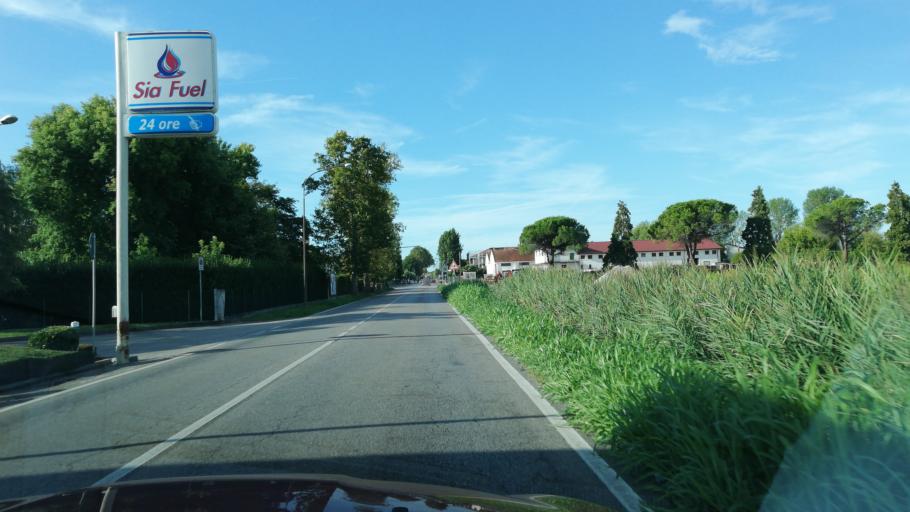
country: IT
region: Veneto
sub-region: Provincia di Venezia
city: La Salute di Livenza
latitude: 45.6615
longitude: 12.8026
